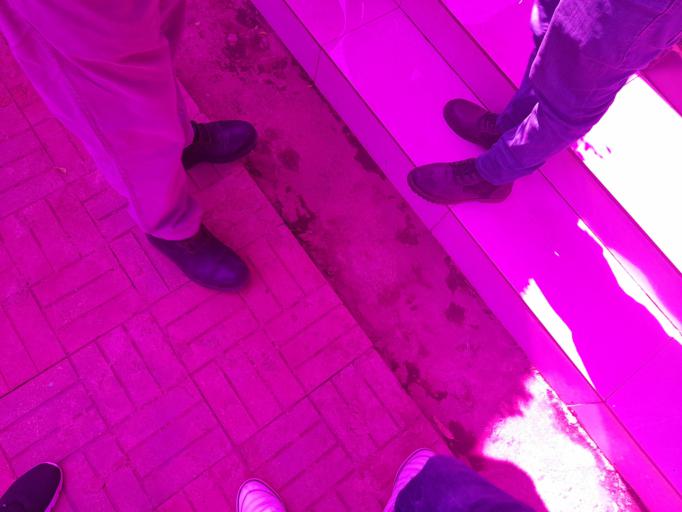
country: ET
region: Oromiya
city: Bedele
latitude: 9.0987
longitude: 36.5392
